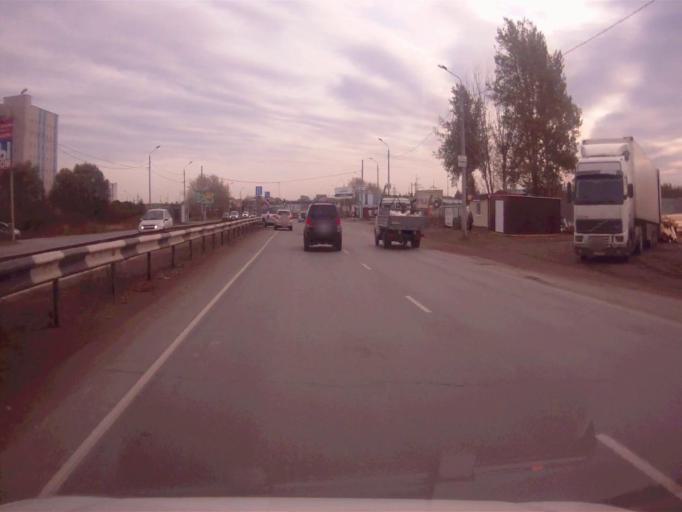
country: RU
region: Chelyabinsk
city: Novosineglazovskiy
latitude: 55.0656
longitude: 61.3962
